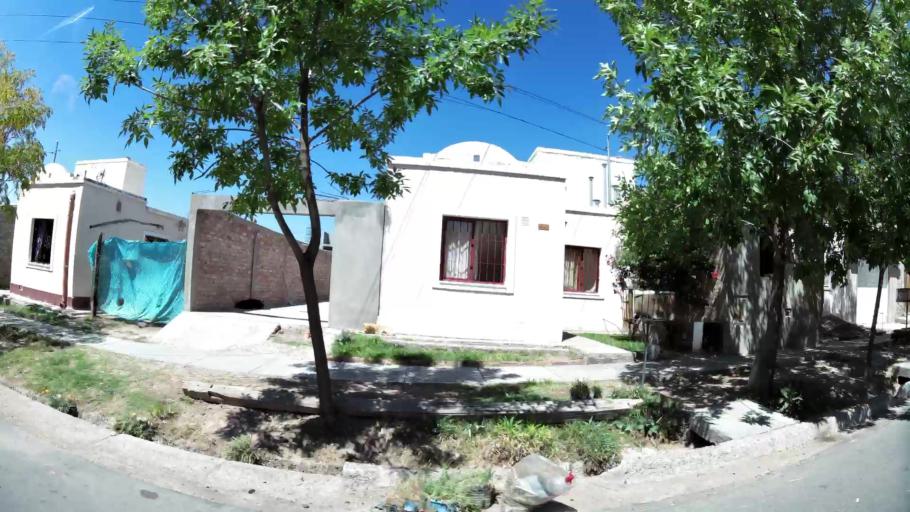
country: AR
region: Mendoza
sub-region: Departamento de Godoy Cruz
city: Godoy Cruz
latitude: -32.9410
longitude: -68.8730
